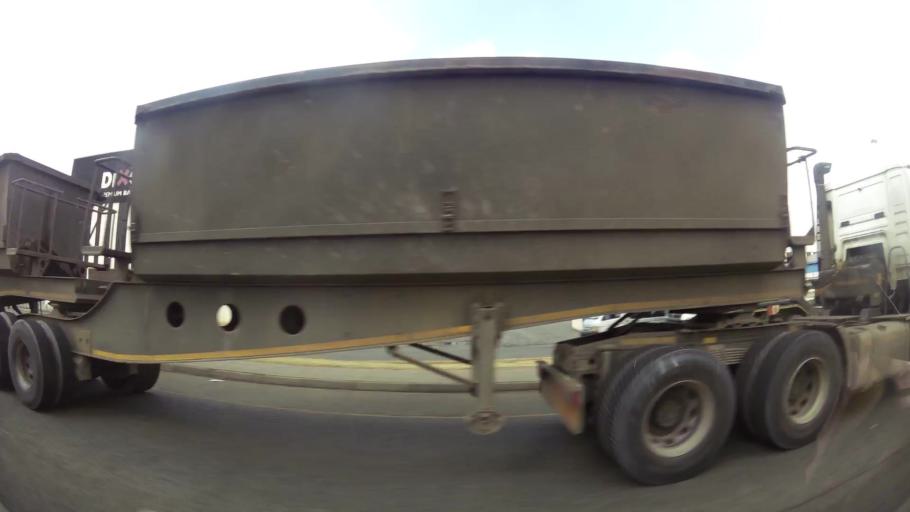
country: ZA
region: Gauteng
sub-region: Sedibeng District Municipality
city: Vereeniging
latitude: -26.6596
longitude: 27.9351
